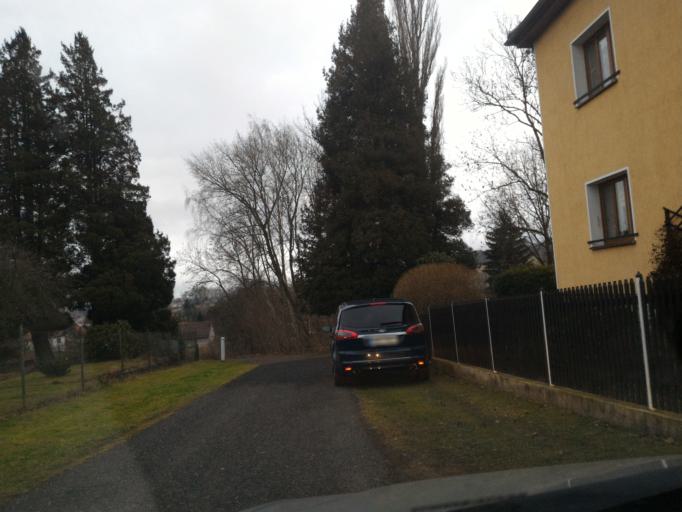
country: CZ
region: Ustecky
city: Varnsdorf
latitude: 50.9070
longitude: 14.6060
